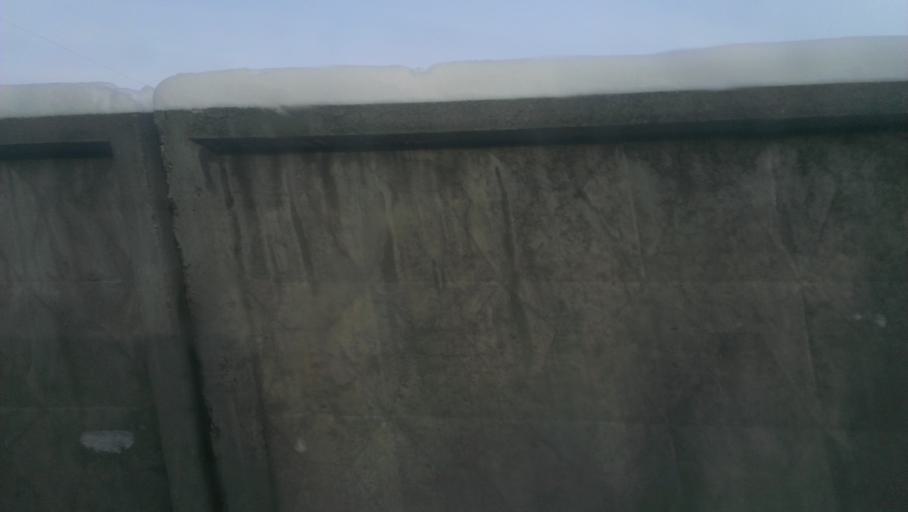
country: RU
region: Altai Krai
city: Nauchnyy Gorodok
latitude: 53.4213
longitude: 83.5219
